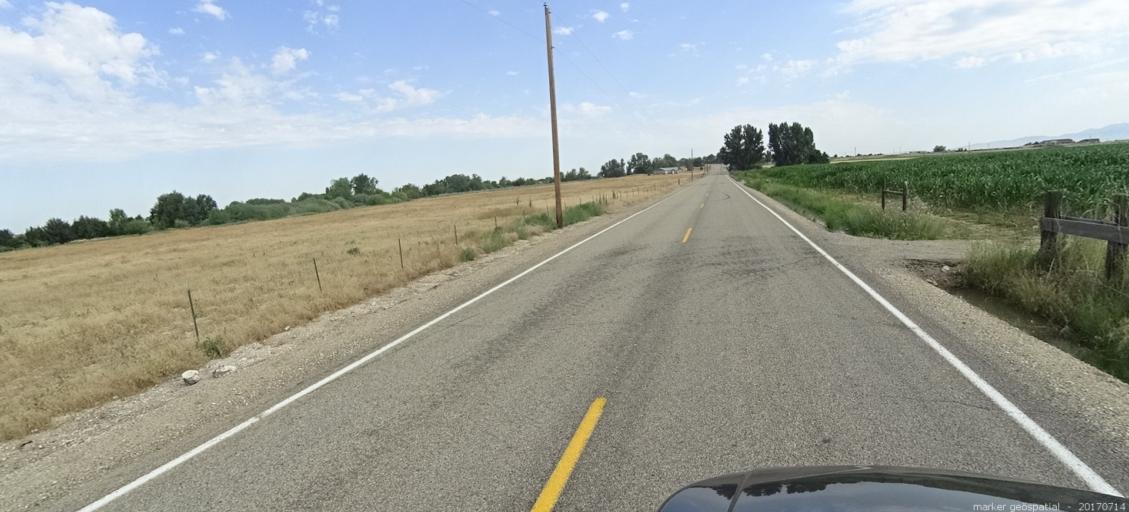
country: US
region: Idaho
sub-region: Ada County
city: Kuna
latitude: 43.4800
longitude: -116.3544
